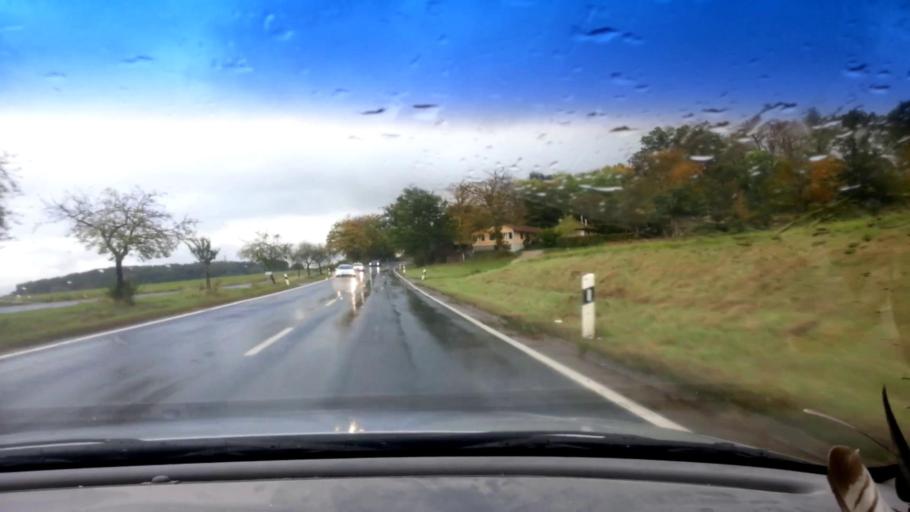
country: DE
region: Bavaria
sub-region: Upper Franconia
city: Burgebrach
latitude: 49.8422
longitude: 10.7326
